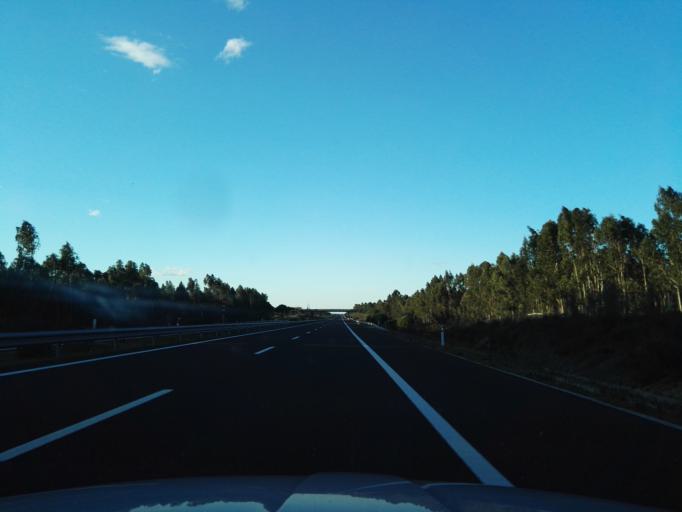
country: PT
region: Santarem
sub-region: Benavente
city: Poceirao
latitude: 38.7932
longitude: -8.6916
